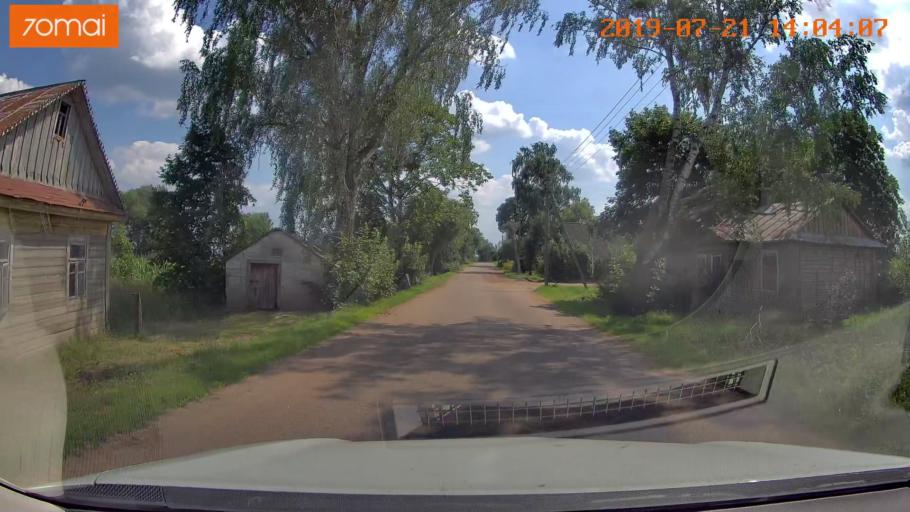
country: BY
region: Grodnenskaya
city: Lyubcha
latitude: 53.7234
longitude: 26.0965
